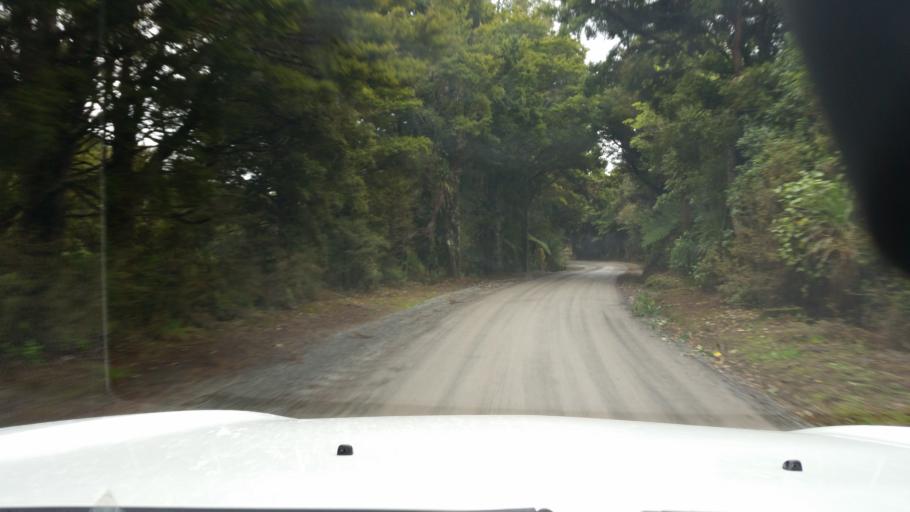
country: NZ
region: Northland
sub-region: Whangarei
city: Whangarei
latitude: -35.7327
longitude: 174.4289
